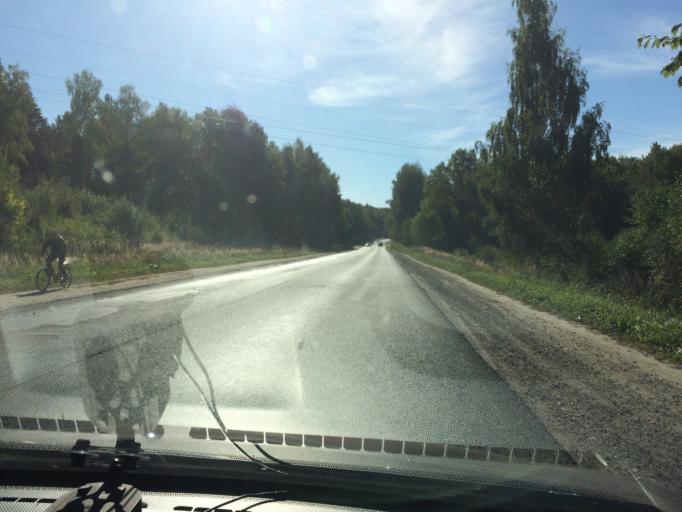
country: RU
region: Mariy-El
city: Yoshkar-Ola
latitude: 56.6101
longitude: 47.9647
